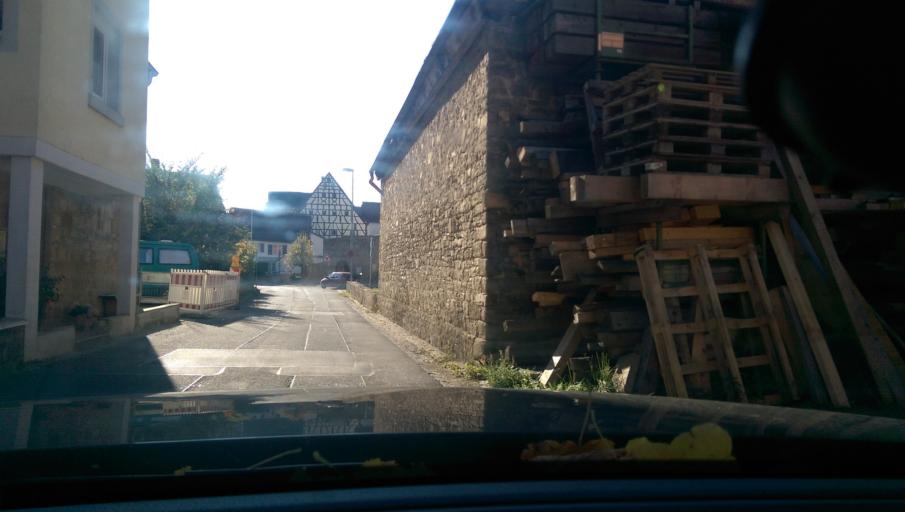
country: DE
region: Bavaria
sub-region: Regierungsbezirk Unterfranken
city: Schonungen
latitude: 50.0577
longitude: 10.2886
